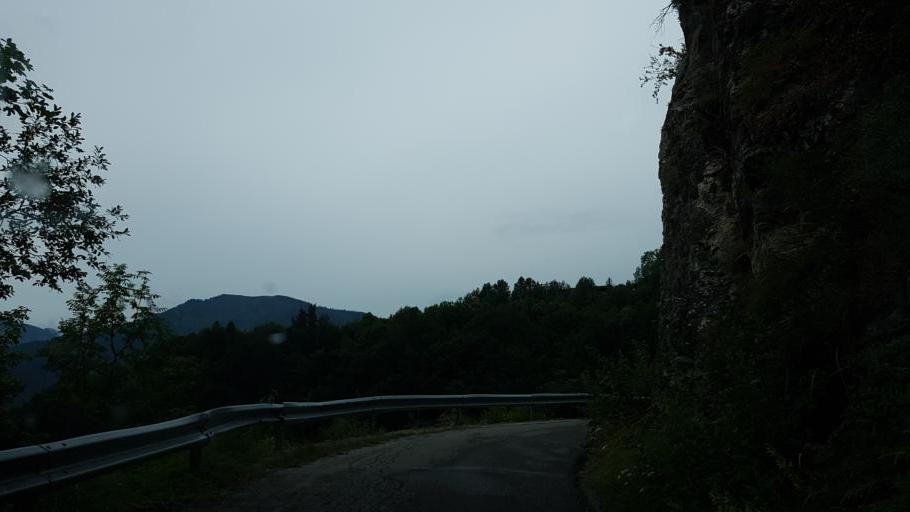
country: IT
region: Piedmont
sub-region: Provincia di Cuneo
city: Stroppo
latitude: 44.5168
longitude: 7.1160
